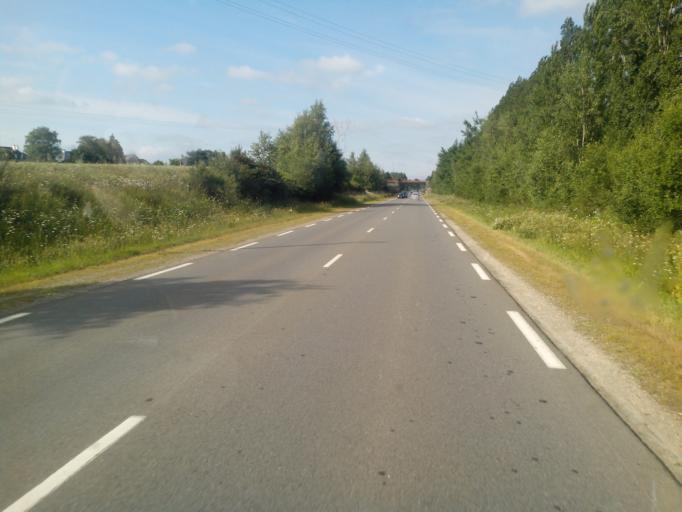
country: FR
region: Brittany
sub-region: Departement d'Ille-et-Vilaine
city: Le Rheu
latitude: 48.0957
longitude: -1.7890
